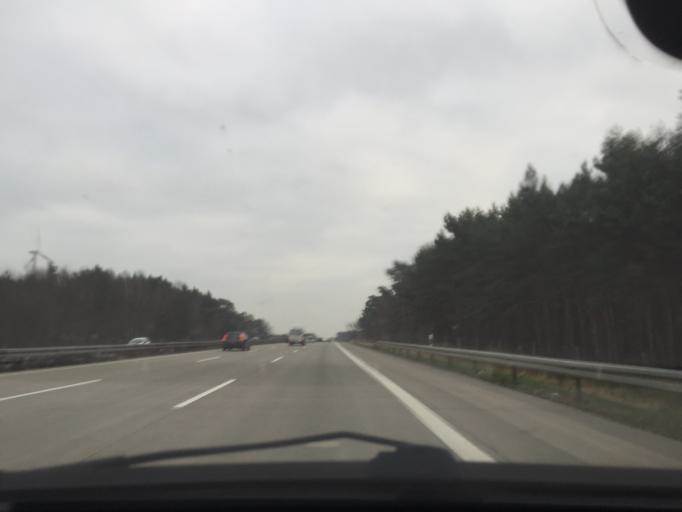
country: DE
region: Saxony-Anhalt
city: Tucheim
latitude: 52.2522
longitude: 12.2198
